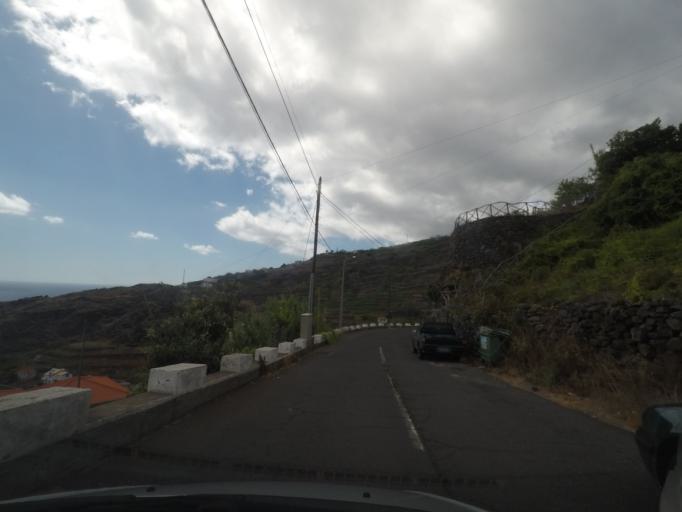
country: PT
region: Madeira
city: Ribeira Brava
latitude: 32.6793
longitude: -17.0720
